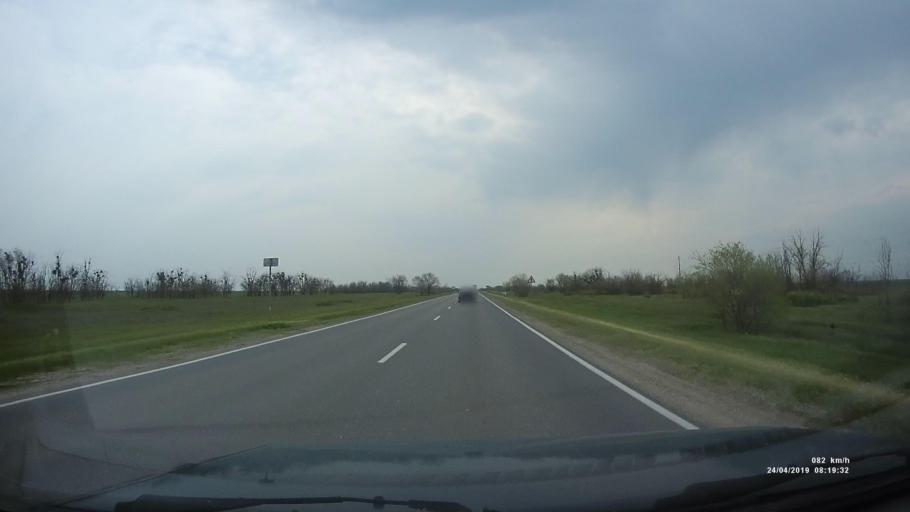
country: RU
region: Kalmykiya
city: Priyutnoye
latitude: 46.1044
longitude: 43.6669
